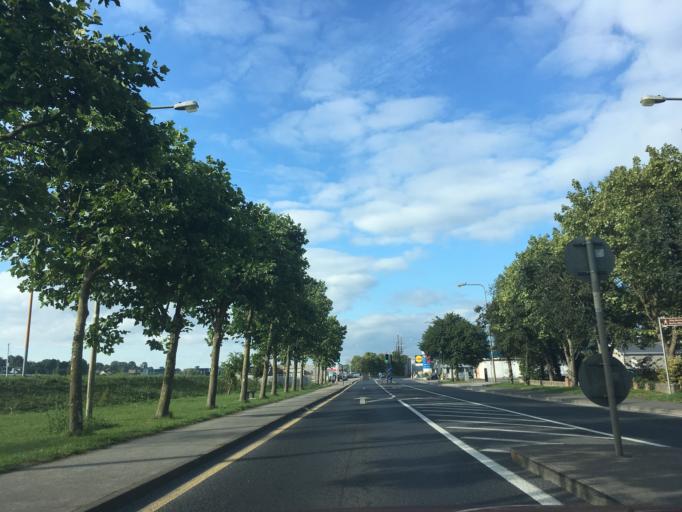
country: IE
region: Leinster
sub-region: Loch Garman
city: New Ross
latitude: 52.3907
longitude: -6.9506
